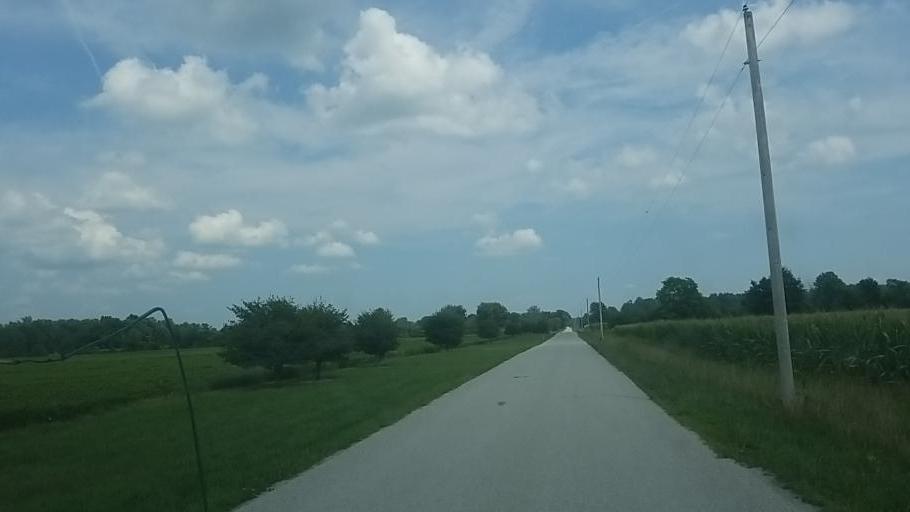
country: US
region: Ohio
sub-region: Hardin County
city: Forest
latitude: 40.7530
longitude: -83.5995
